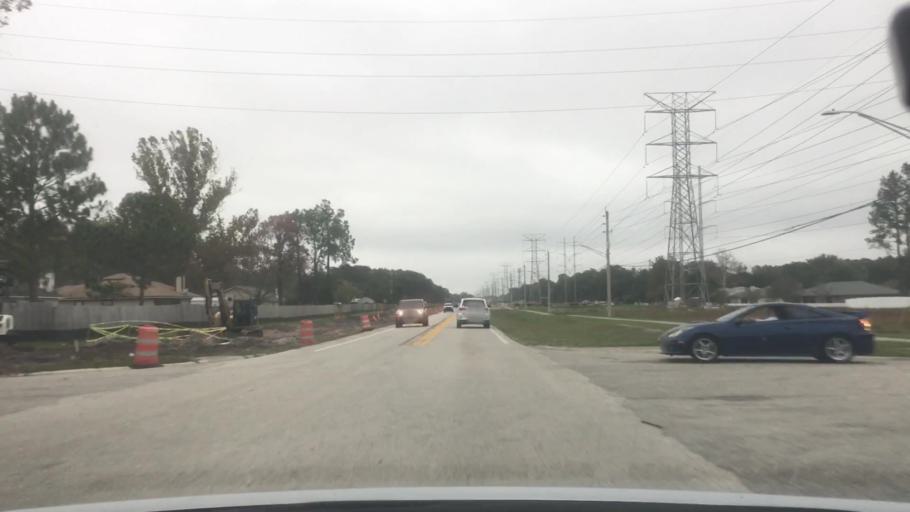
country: US
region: Florida
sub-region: Duval County
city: Atlantic Beach
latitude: 30.3480
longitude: -81.4899
